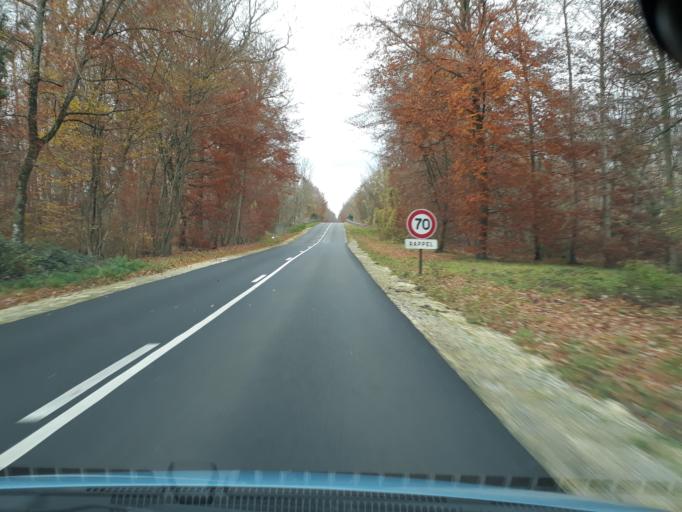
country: FR
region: Ile-de-France
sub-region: Departement de Seine-et-Marne
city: Thomery
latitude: 48.3927
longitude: 2.7707
